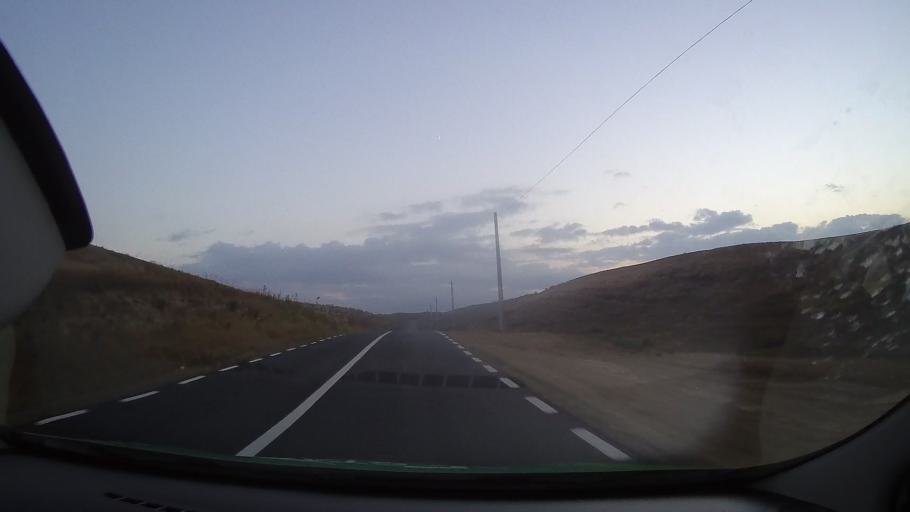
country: RO
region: Constanta
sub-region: Comuna Oltina
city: Oltina
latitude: 44.1455
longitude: 27.6665
